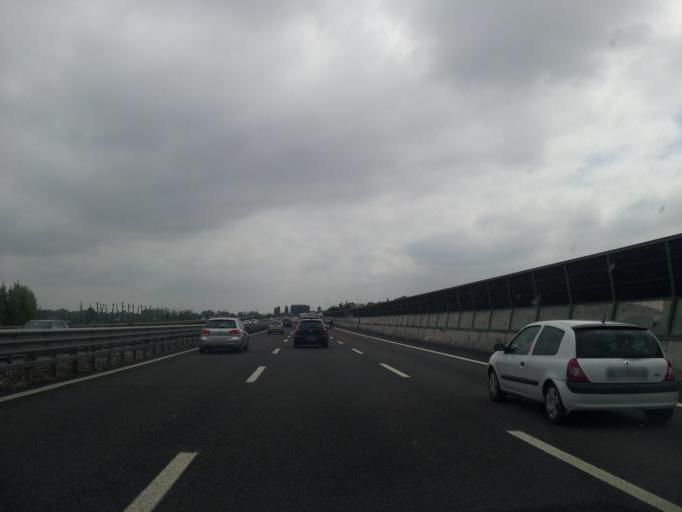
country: IT
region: Veneto
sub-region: Provincia di Vicenza
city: Arcugnano-Torri
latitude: 45.5164
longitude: 11.5705
